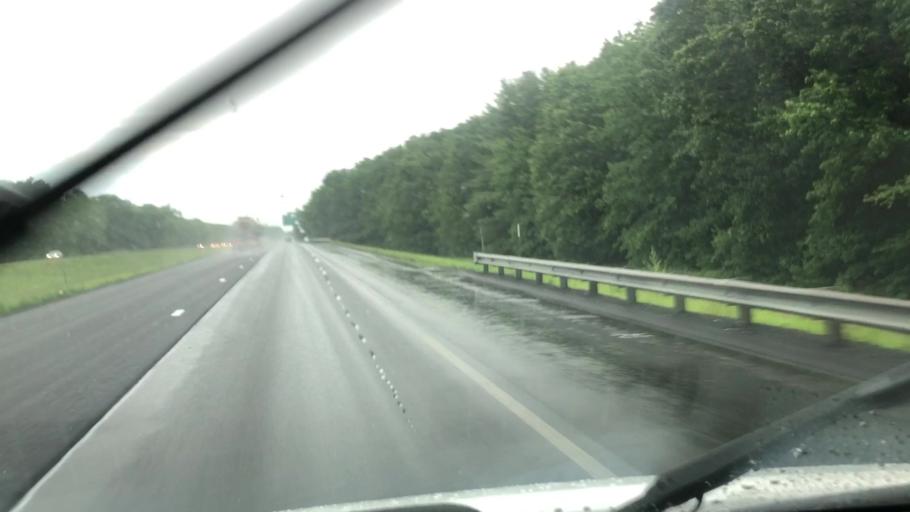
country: US
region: Massachusetts
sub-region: Hampshire County
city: Hatfield
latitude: 42.3882
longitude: -72.6299
